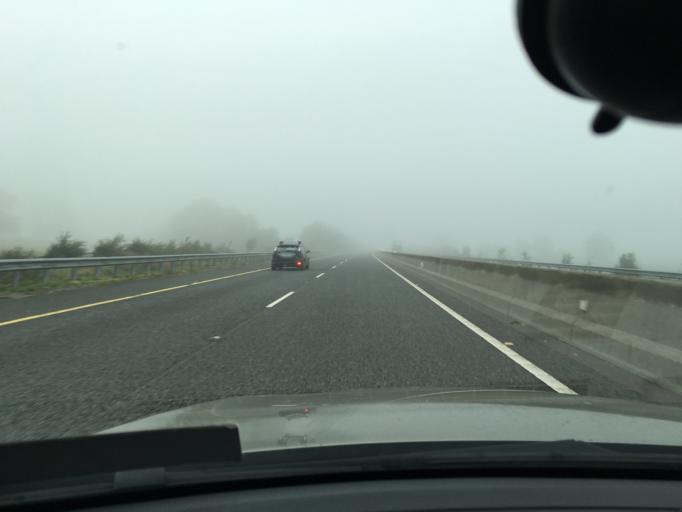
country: IE
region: Leinster
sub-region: An Iarmhi
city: Kilbeggan
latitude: 53.3752
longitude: -7.5527
